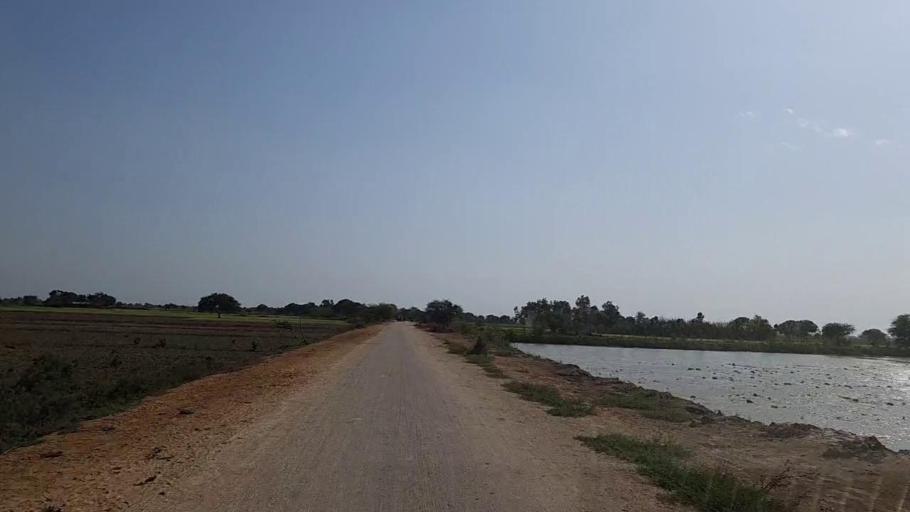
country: PK
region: Sindh
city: Daro Mehar
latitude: 24.7600
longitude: 68.1828
